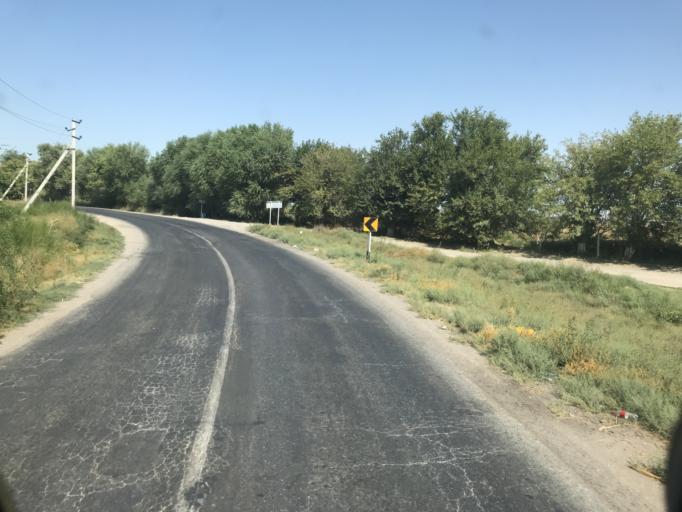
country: KZ
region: Ongtustik Qazaqstan
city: Ilyich
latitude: 40.9483
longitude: 68.4890
